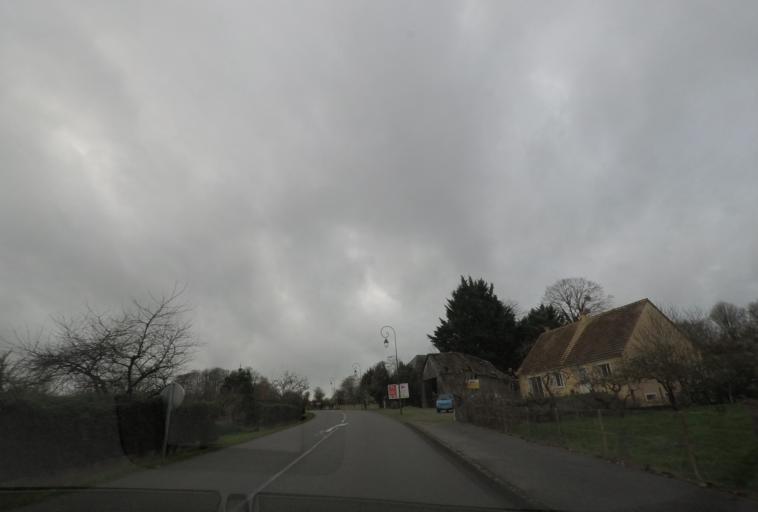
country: FR
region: Pays de la Loire
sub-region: Departement de la Sarthe
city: Vibraye
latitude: 47.9927
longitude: 0.7639
